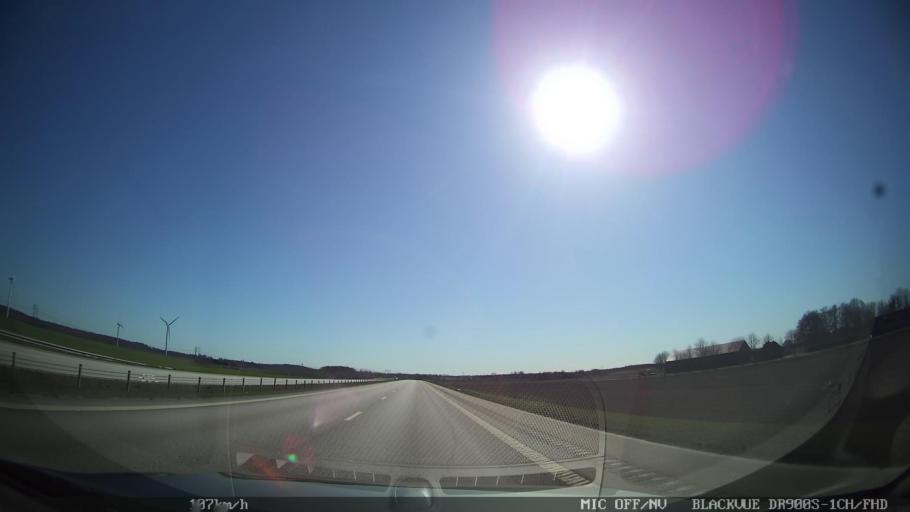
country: SE
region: Skane
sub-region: Malmo
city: Oxie
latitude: 55.5381
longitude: 13.1675
